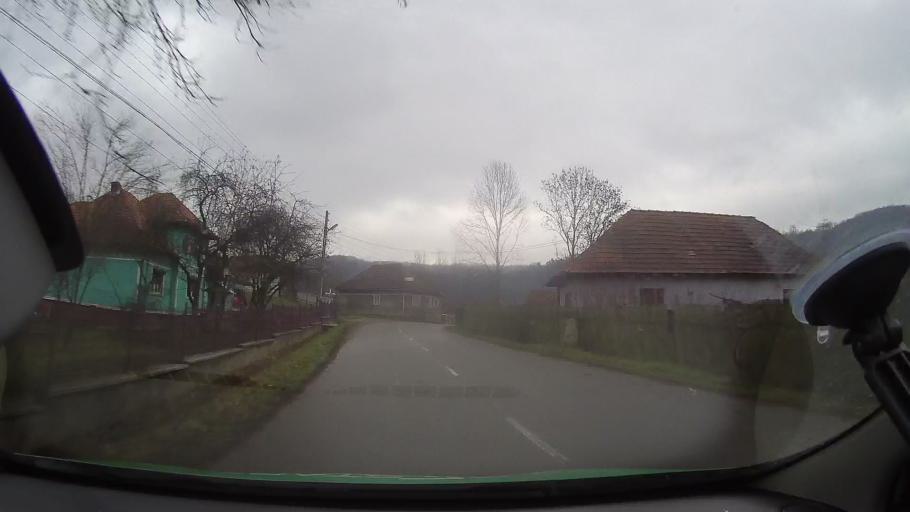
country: RO
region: Hunedoara
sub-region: Comuna Tomesti
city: Tomesti
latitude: 46.1994
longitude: 22.6497
